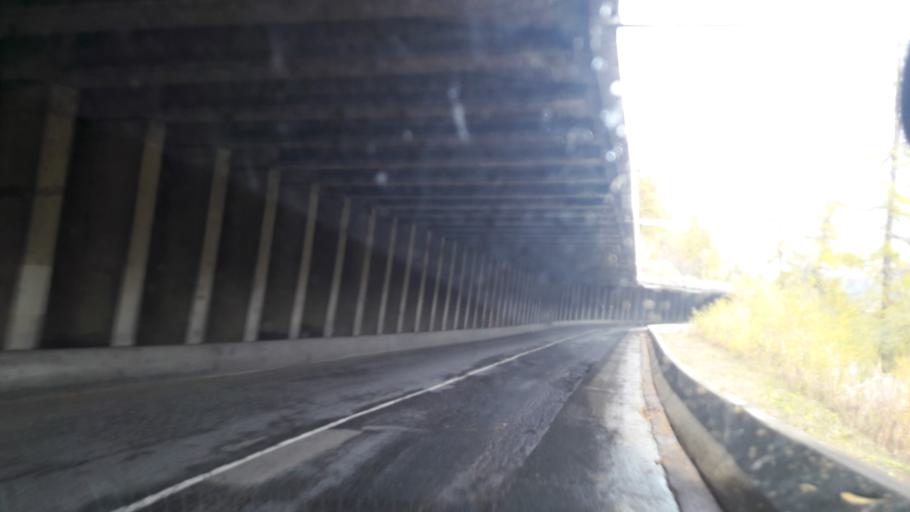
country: FR
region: Rhone-Alpes
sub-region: Departement de la Savoie
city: Tignes
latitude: 45.4877
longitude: 6.9266
